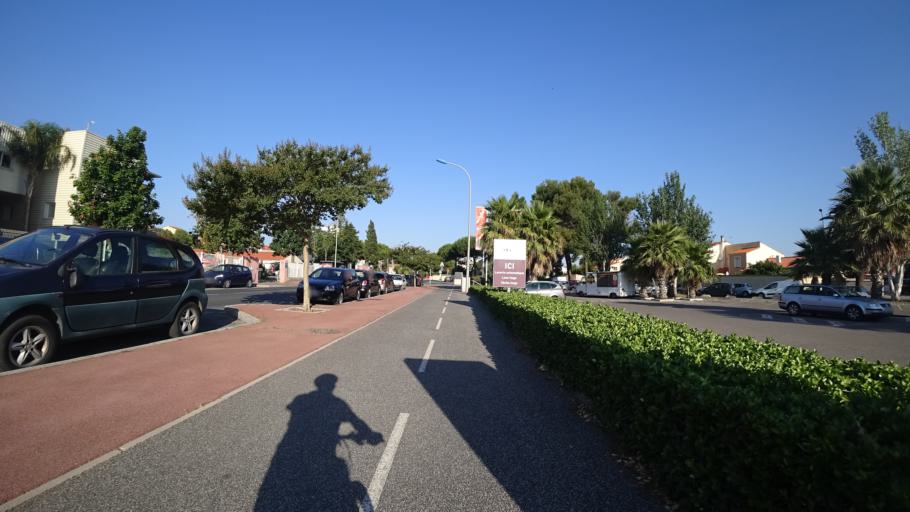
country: FR
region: Languedoc-Roussillon
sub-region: Departement des Pyrenees-Orientales
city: Canet-en-Roussillon
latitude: 42.7060
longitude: 3.0137
